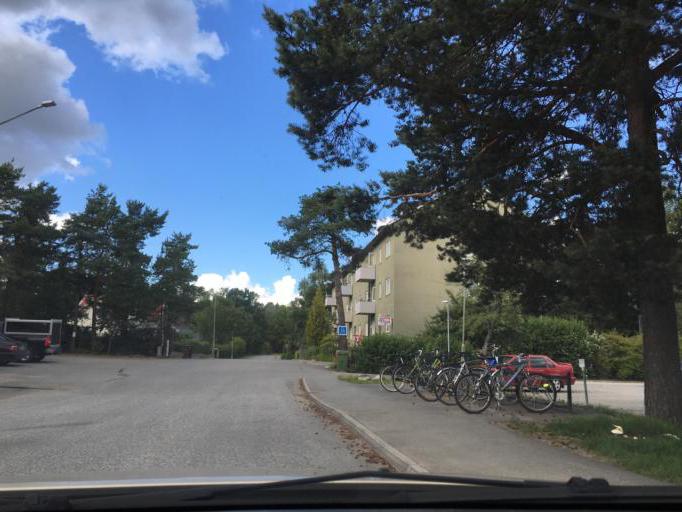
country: SE
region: Stockholm
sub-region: Nacka Kommun
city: Boo
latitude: 59.3190
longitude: 18.2433
